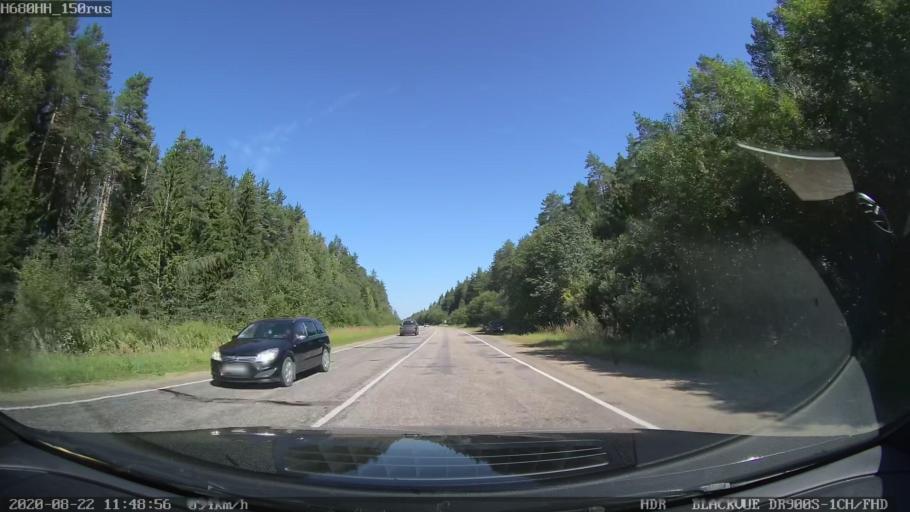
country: RU
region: Tverskaya
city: Sakharovo
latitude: 57.0692
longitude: 36.1091
